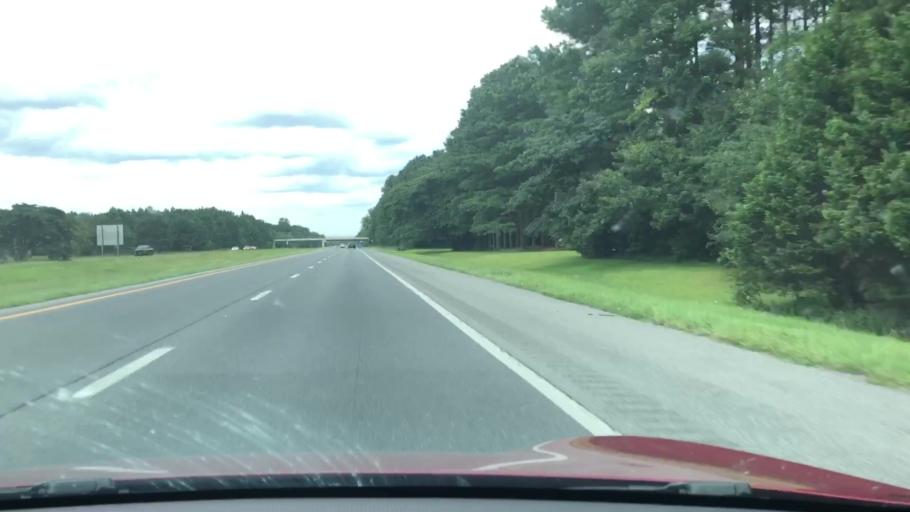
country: US
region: Maryland
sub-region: Wicomico County
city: Fruitland
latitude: 38.3173
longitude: -75.5897
